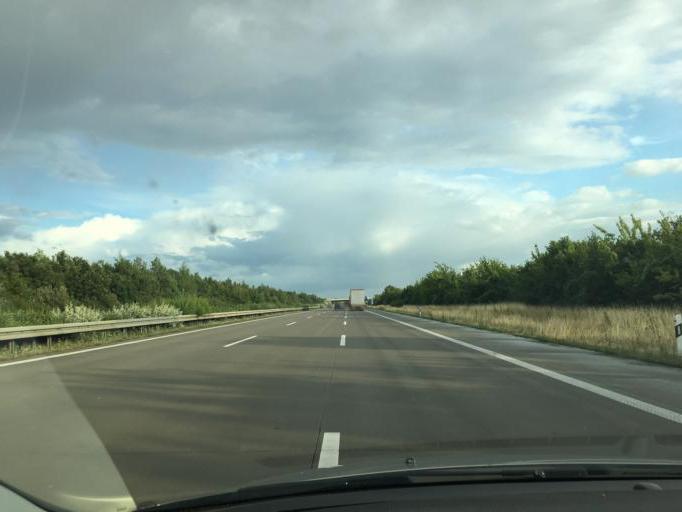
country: DE
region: Saxony
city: Wiedemar
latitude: 51.4710
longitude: 12.2156
